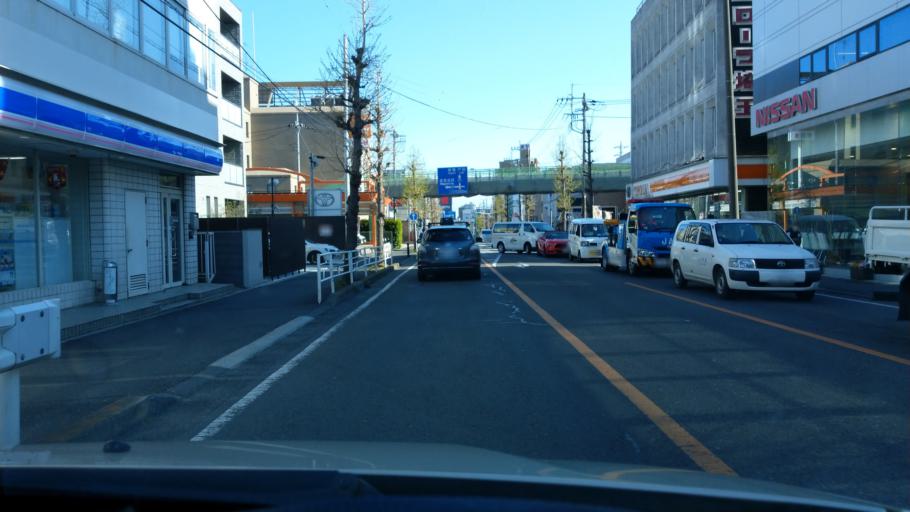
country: JP
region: Saitama
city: Yono
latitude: 35.8885
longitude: 139.6298
